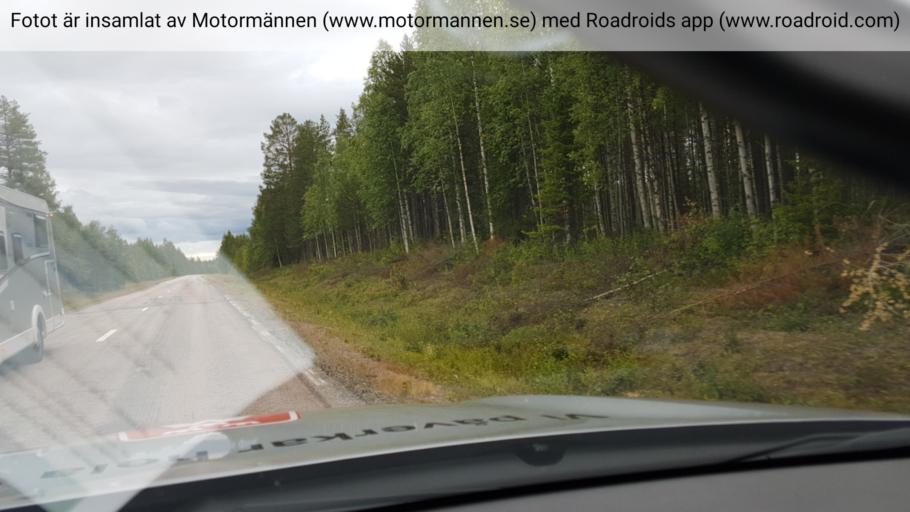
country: SE
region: Norrbotten
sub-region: Overkalix Kommun
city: OEverkalix
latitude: 66.8103
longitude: 22.9920
